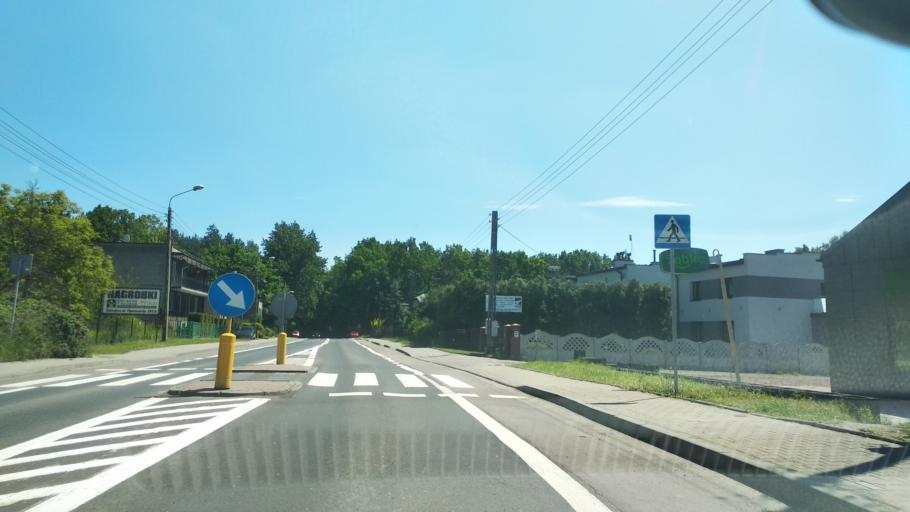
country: PL
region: Silesian Voivodeship
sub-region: Ruda Slaska
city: Ruda Slaska
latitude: 50.2379
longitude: 18.9088
